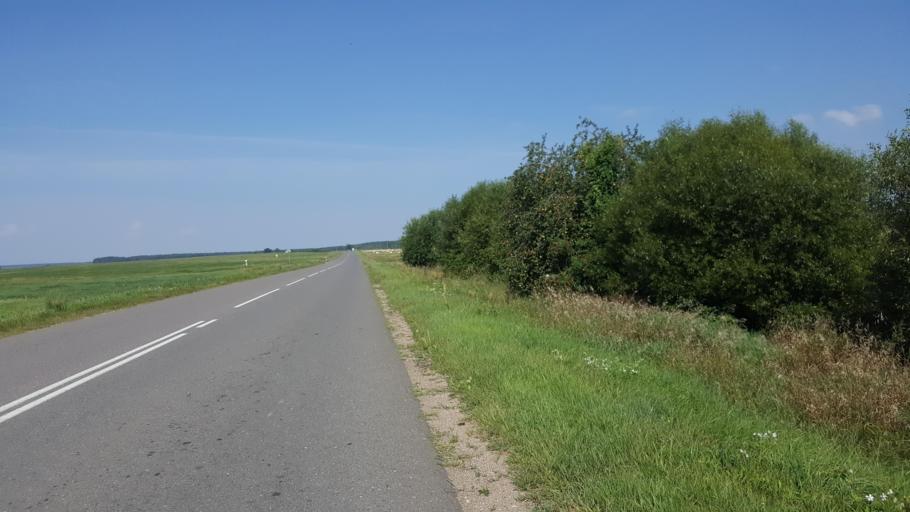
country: BY
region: Brest
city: Kamyanyuki
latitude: 52.4923
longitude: 23.6820
